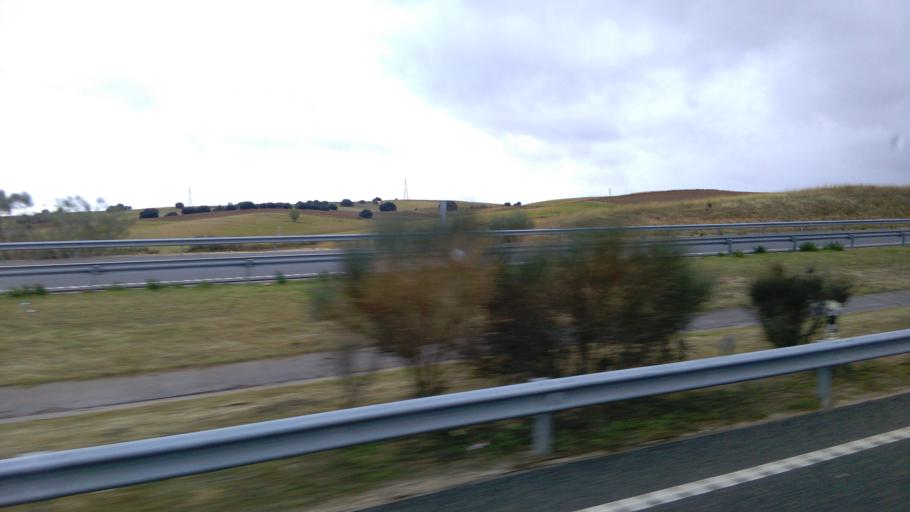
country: ES
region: Madrid
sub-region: Provincia de Madrid
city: Arroyomolinos
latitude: 40.2553
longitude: -3.9171
